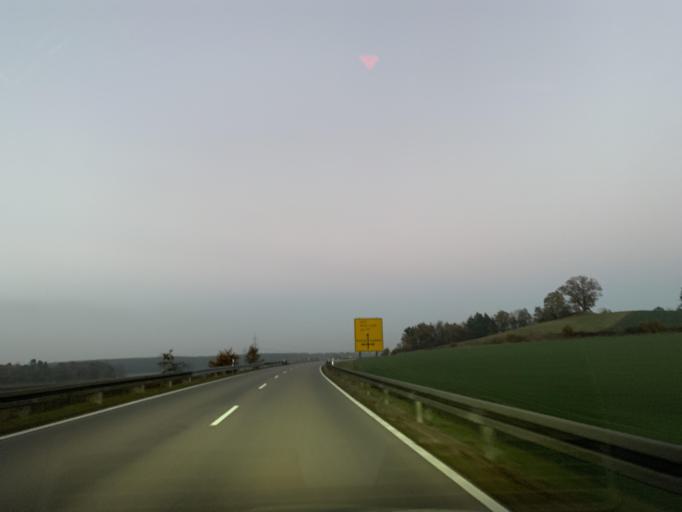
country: DE
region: Bavaria
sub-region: Upper Palatinate
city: Brunn
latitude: 49.2366
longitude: 12.1736
